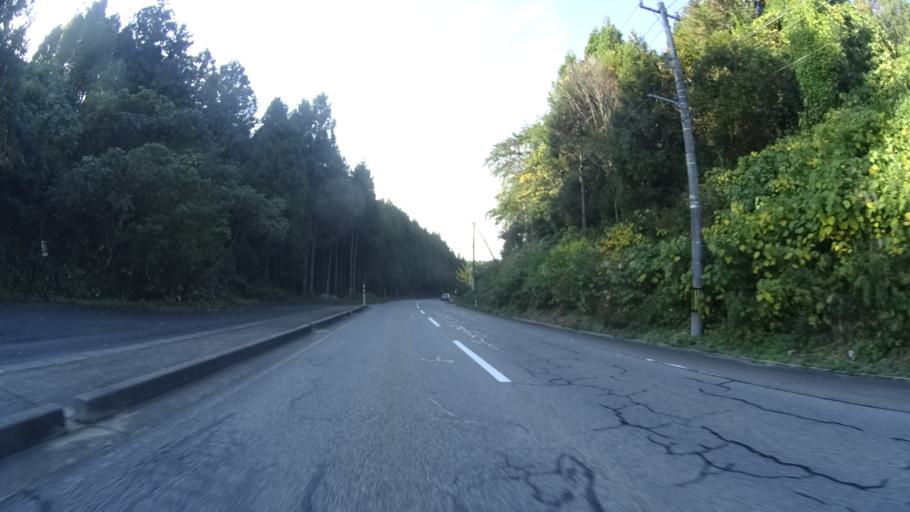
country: JP
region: Ishikawa
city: Hakui
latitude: 37.0060
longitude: 136.8024
